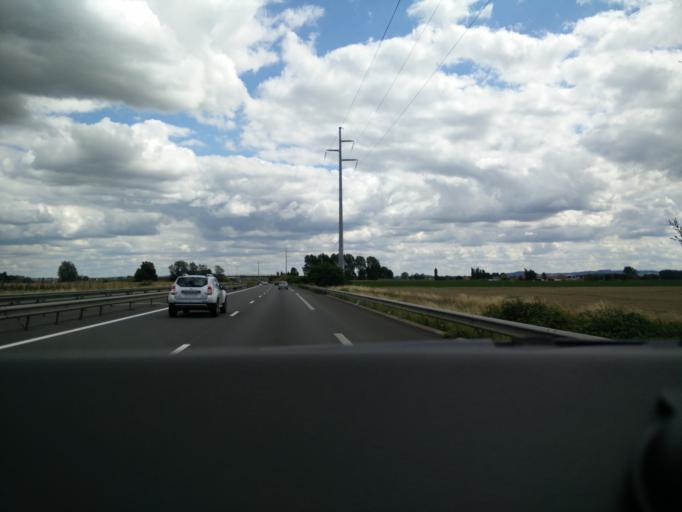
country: FR
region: Nord-Pas-de-Calais
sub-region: Departement du Nord
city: Wormhout
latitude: 50.9109
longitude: 2.4842
